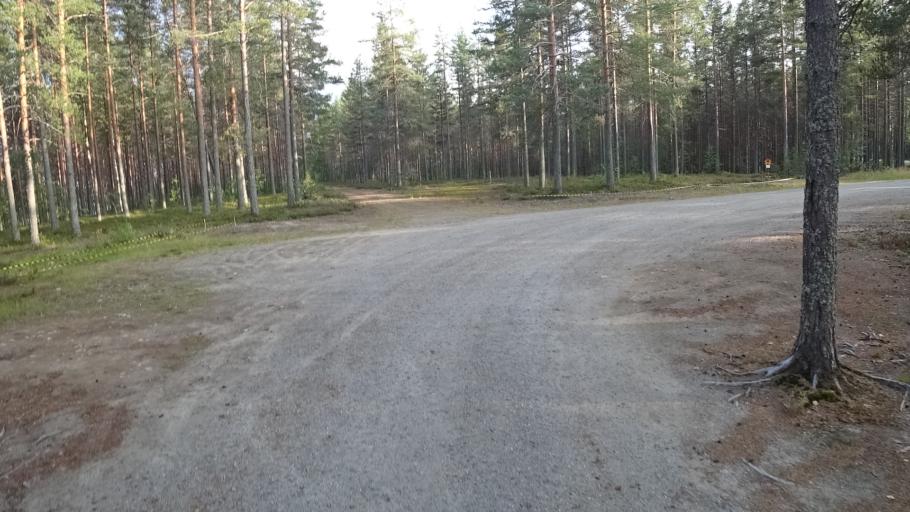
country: FI
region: North Karelia
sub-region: Joensuu
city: Ilomantsi
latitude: 62.6525
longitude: 31.0624
